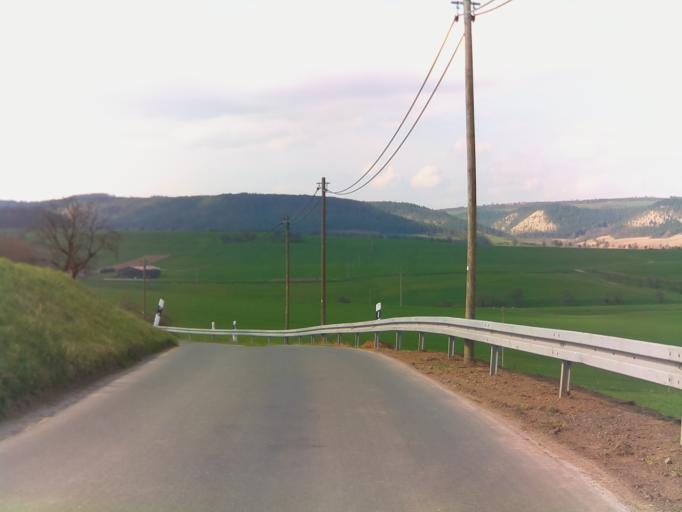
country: DE
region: Thuringia
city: Kahla
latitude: 50.8201
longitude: 11.5690
